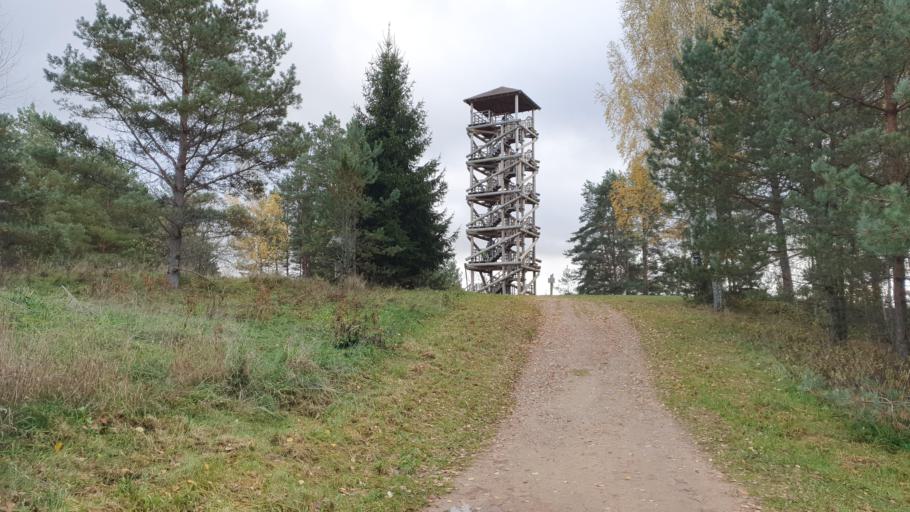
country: LV
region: Daugavpils
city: Daugavpils
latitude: 55.9154
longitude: 26.8150
